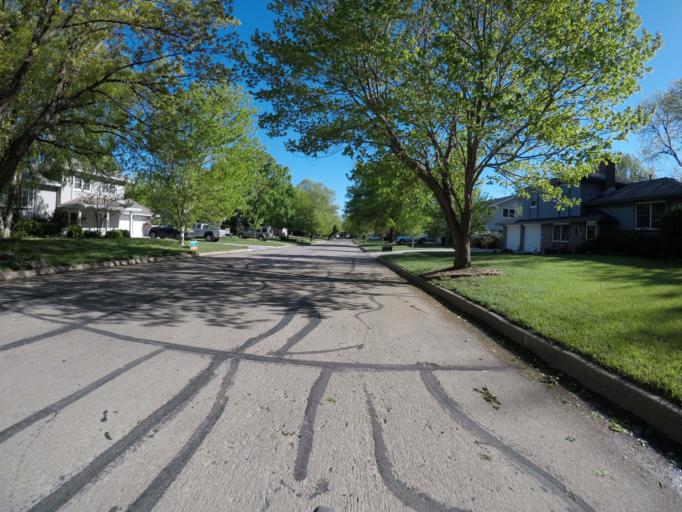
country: US
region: Kansas
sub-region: Riley County
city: Manhattan
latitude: 39.2012
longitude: -96.6117
